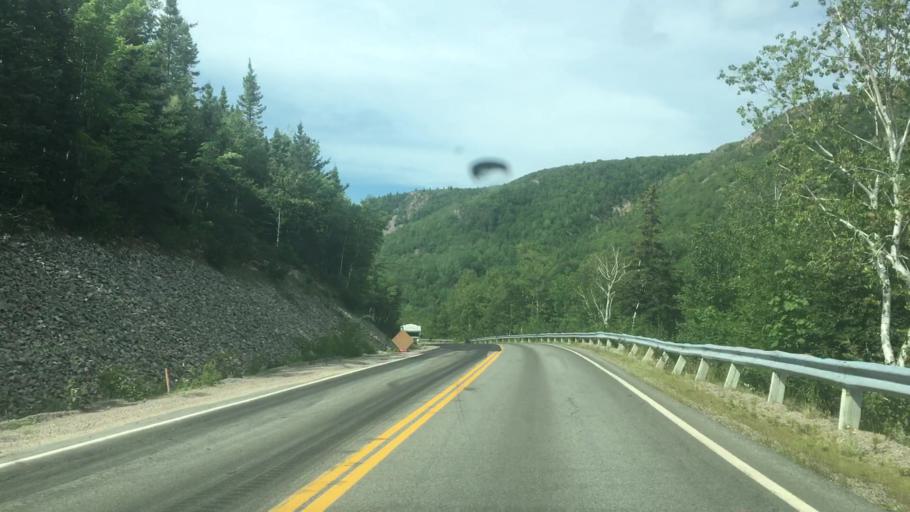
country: CA
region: Nova Scotia
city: Sydney Mines
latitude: 46.5795
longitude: -60.3900
